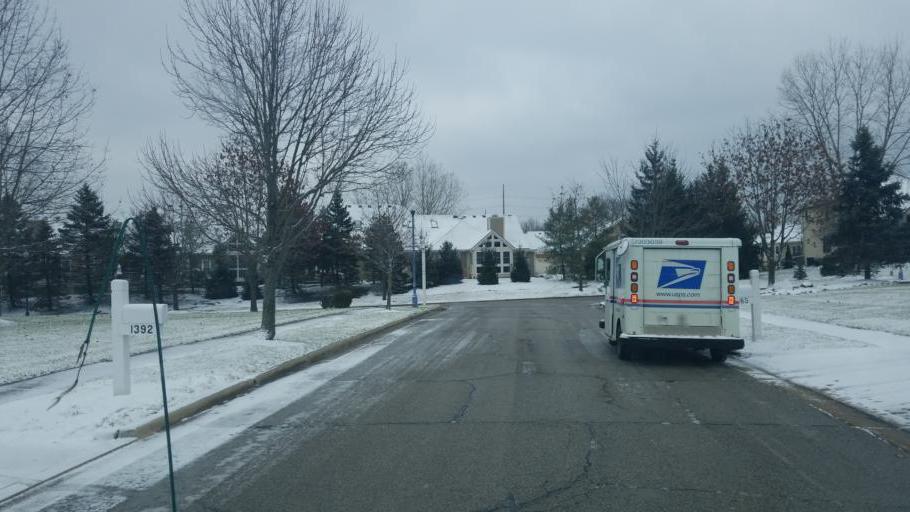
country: US
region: Ohio
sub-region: Franklin County
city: New Albany
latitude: 40.0510
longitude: -82.8299
